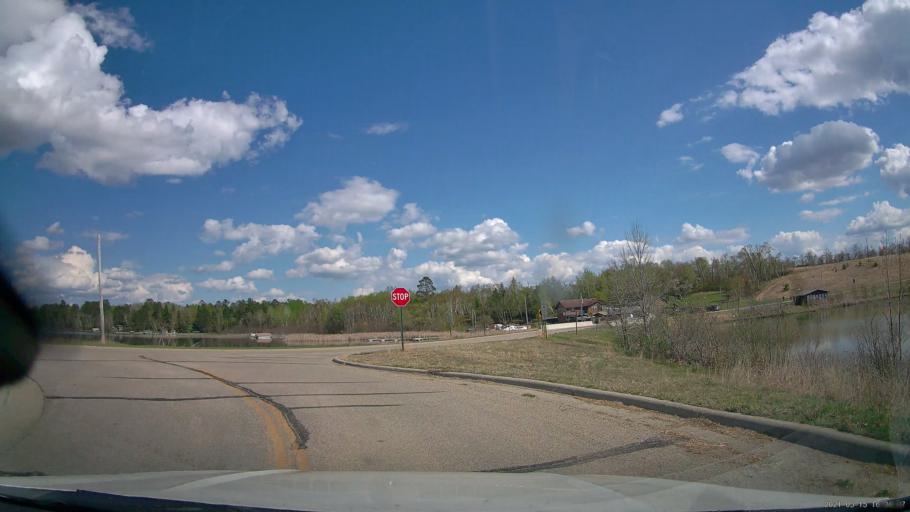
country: US
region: Minnesota
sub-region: Hubbard County
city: Park Rapids
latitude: 46.9795
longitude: -94.9511
